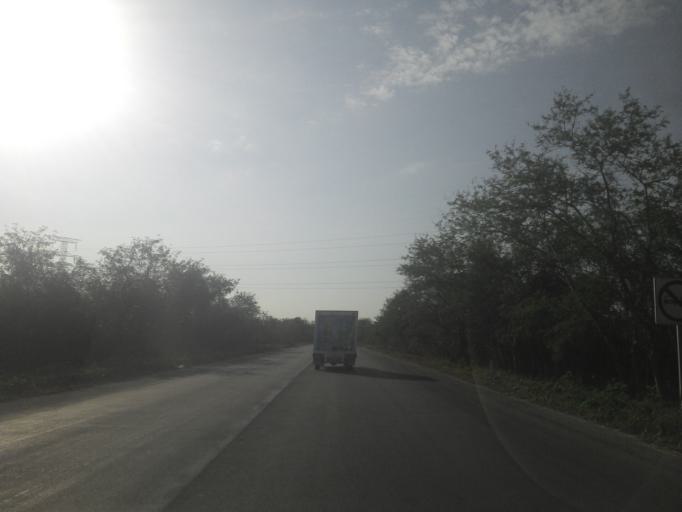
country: MX
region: Yucatan
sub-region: Valladolid
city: Tesoco
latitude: 20.7075
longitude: -88.1616
